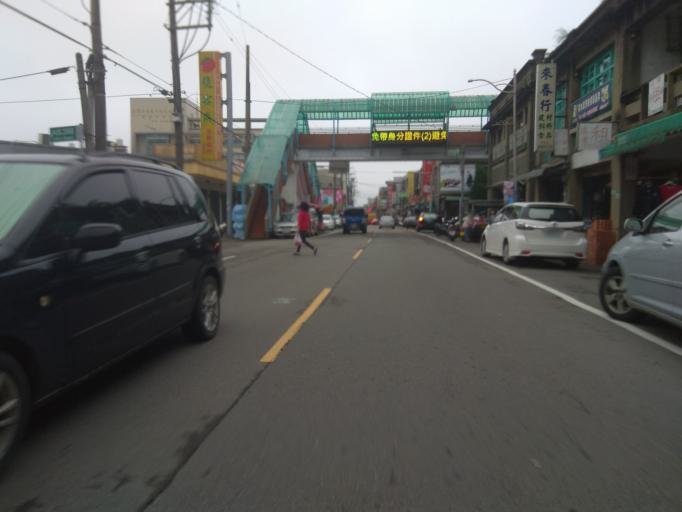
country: TW
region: Taiwan
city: Taoyuan City
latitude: 25.0121
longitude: 121.1375
